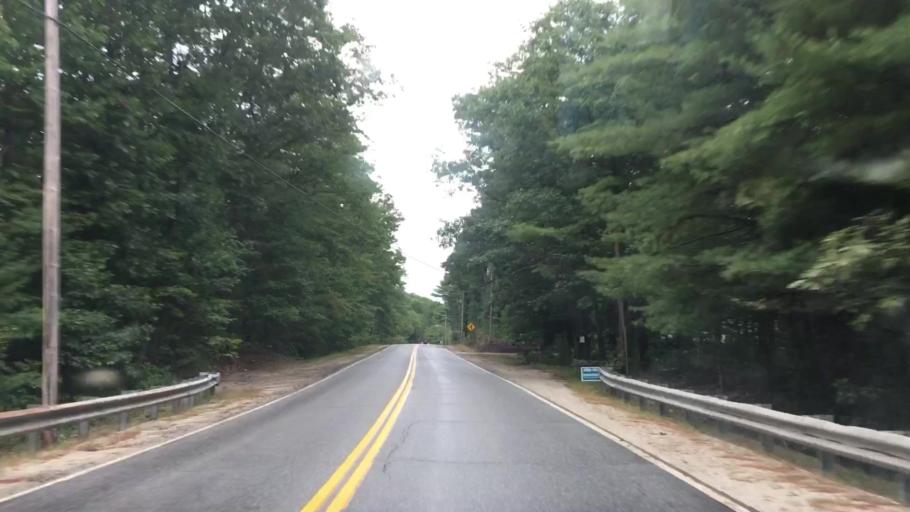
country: US
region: Maine
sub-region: Cumberland County
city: Raymond
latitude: 43.9500
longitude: -70.4629
